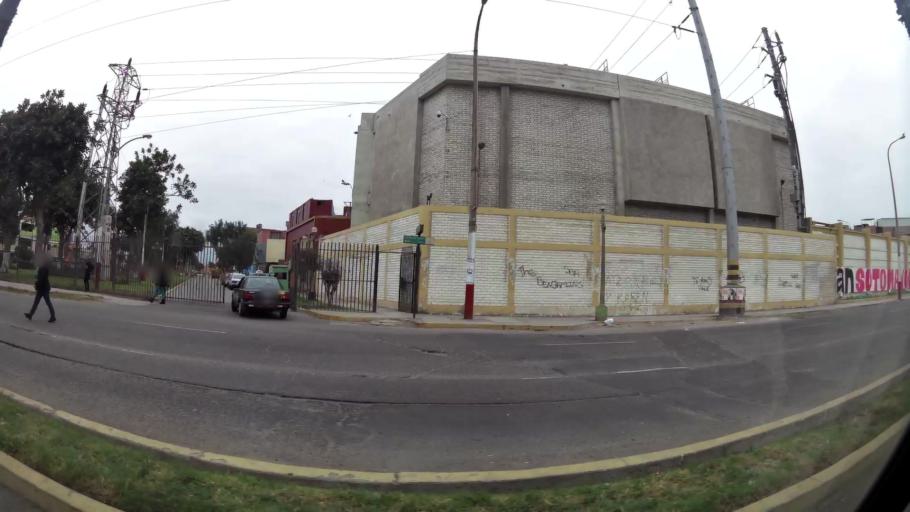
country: PE
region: Callao
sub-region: Callao
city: Callao
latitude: -12.0552
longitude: -77.1333
